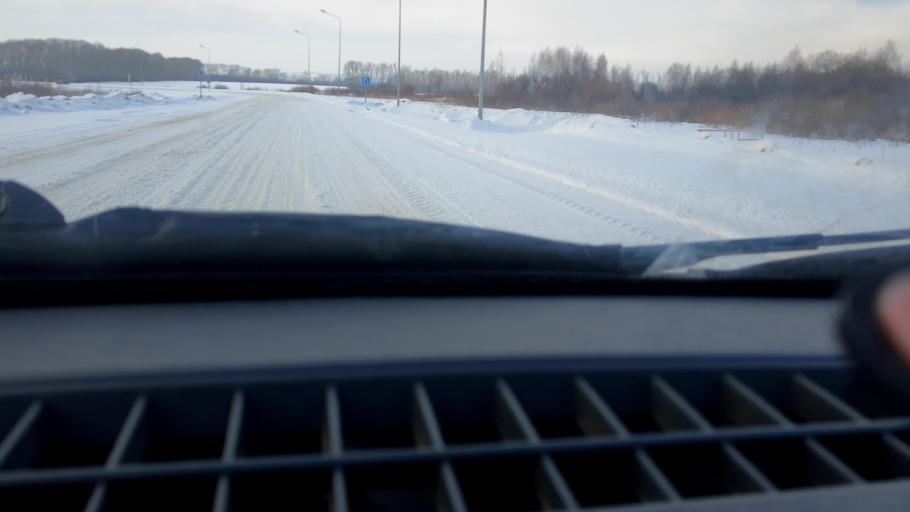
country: RU
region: Bashkortostan
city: Kushnarenkovo
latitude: 55.0634
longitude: 55.4265
